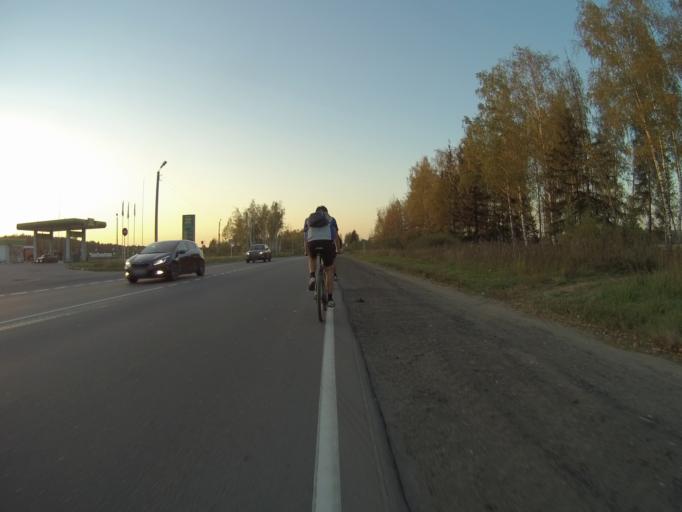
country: RU
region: Vladimir
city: Kommunar
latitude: 56.0335
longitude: 40.5588
